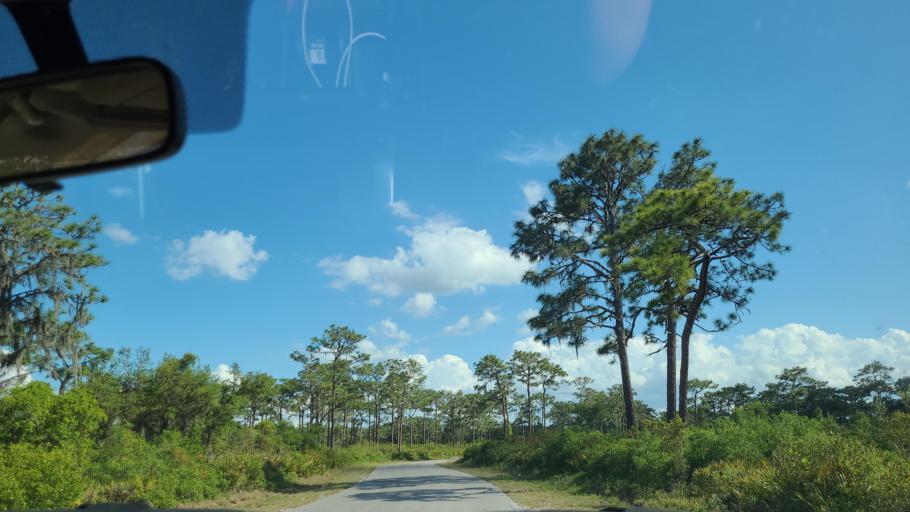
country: US
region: Florida
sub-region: Osceola County
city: Poinciana
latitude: 27.9675
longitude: -81.3799
